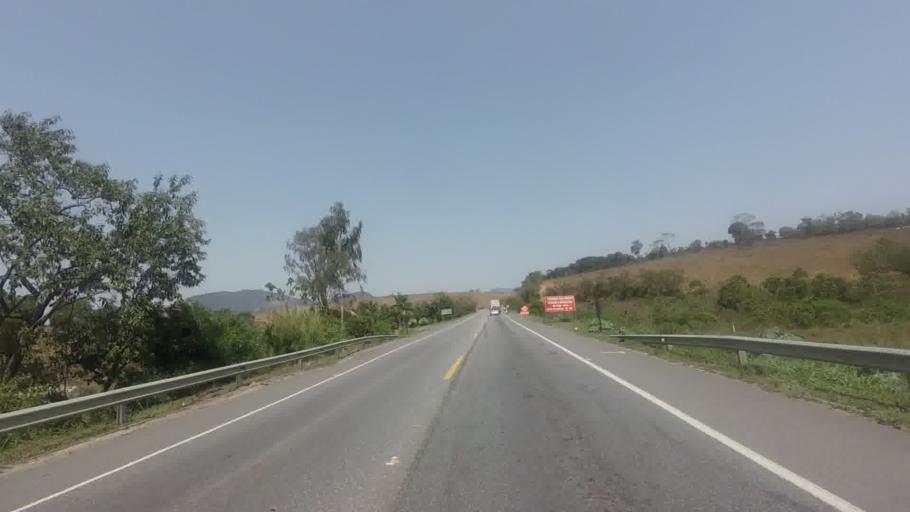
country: BR
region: Espirito Santo
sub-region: Alfredo Chaves
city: Alfredo Chaves
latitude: -20.7143
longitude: -40.7269
